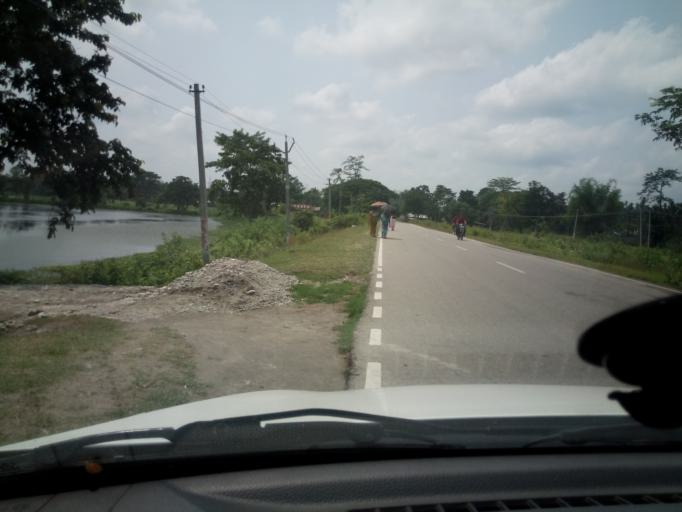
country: IN
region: Assam
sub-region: Udalguri
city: Udalguri
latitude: 26.7190
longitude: 92.1958
